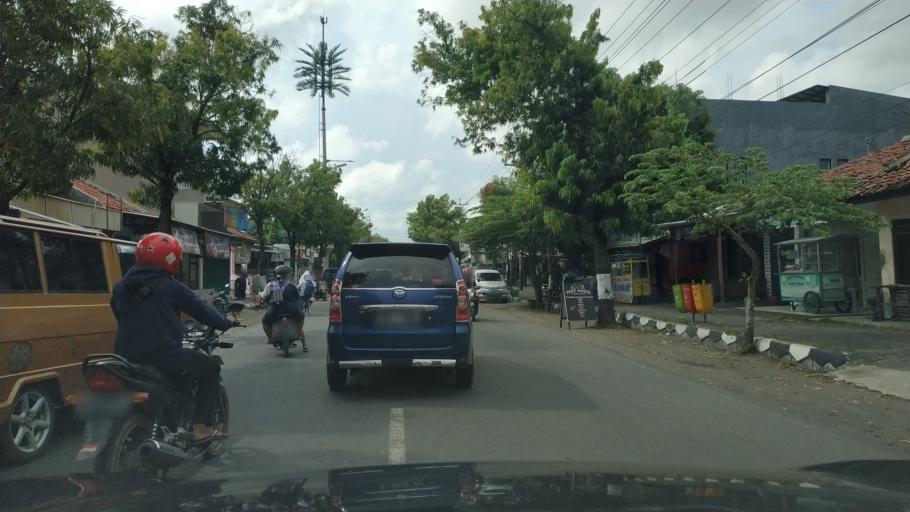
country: ID
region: Central Java
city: Pemalang
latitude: -6.9008
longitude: 109.3833
